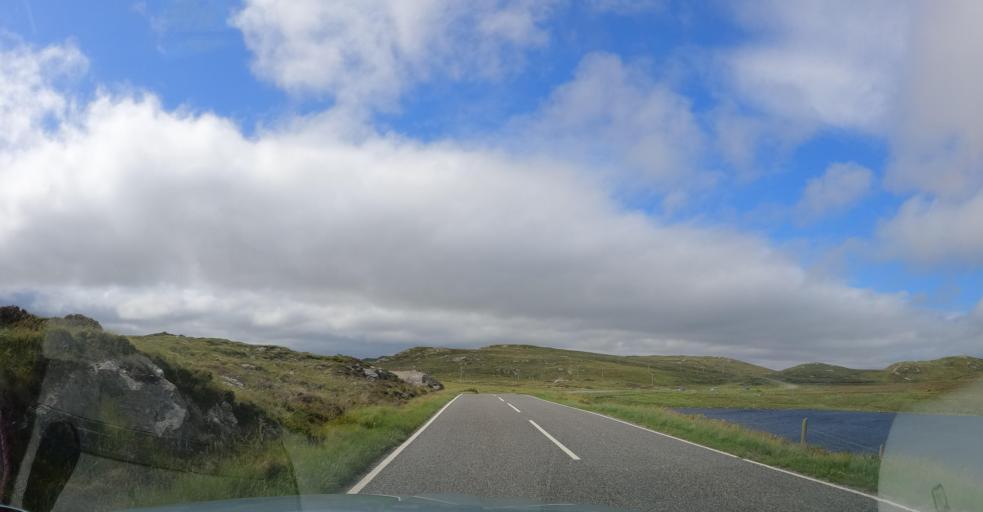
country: GB
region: Scotland
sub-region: Eilean Siar
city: Stornoway
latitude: 58.1178
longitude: -6.5115
